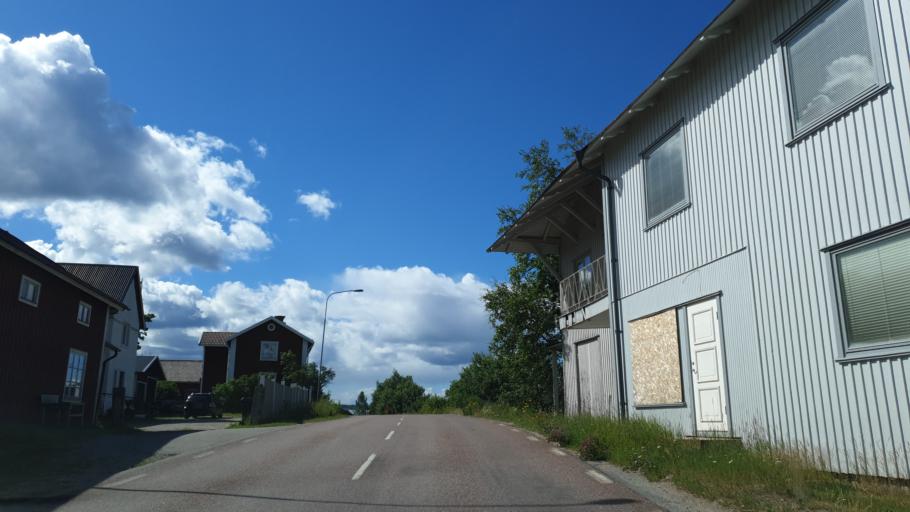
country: SE
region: Gaevleborg
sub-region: Nordanstigs Kommun
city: Bergsjoe
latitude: 62.0498
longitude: 17.2269
